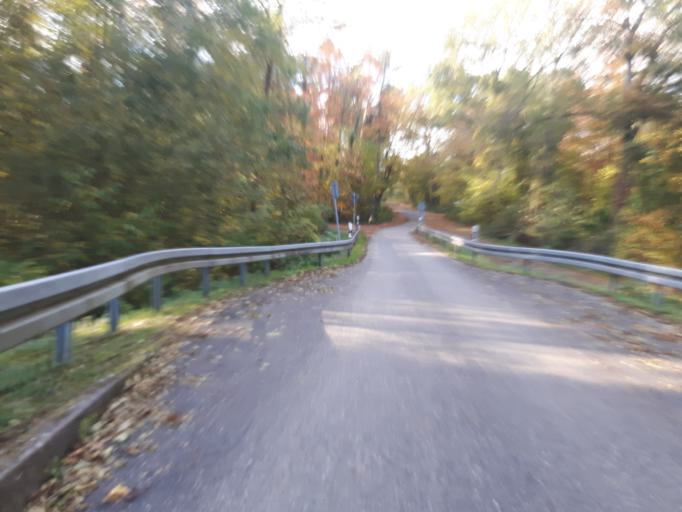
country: DE
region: Baden-Wuerttemberg
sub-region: Karlsruhe Region
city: Malsch
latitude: 49.2629
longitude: 8.6556
